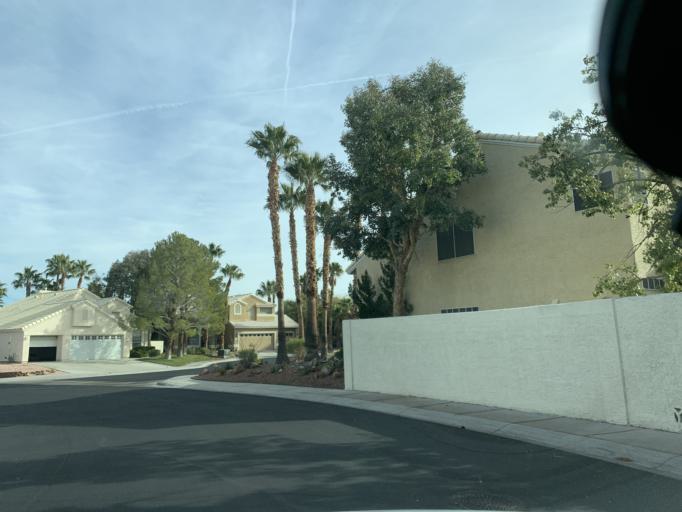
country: US
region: Nevada
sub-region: Clark County
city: Summerlin South
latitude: 36.1533
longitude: -115.2978
